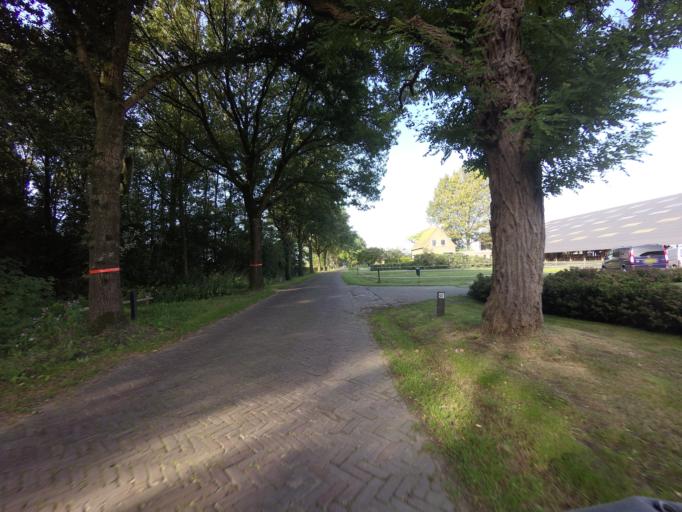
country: NL
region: Friesland
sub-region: Gemeente Weststellingwerf
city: Noordwolde
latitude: 52.9108
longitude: 6.1275
